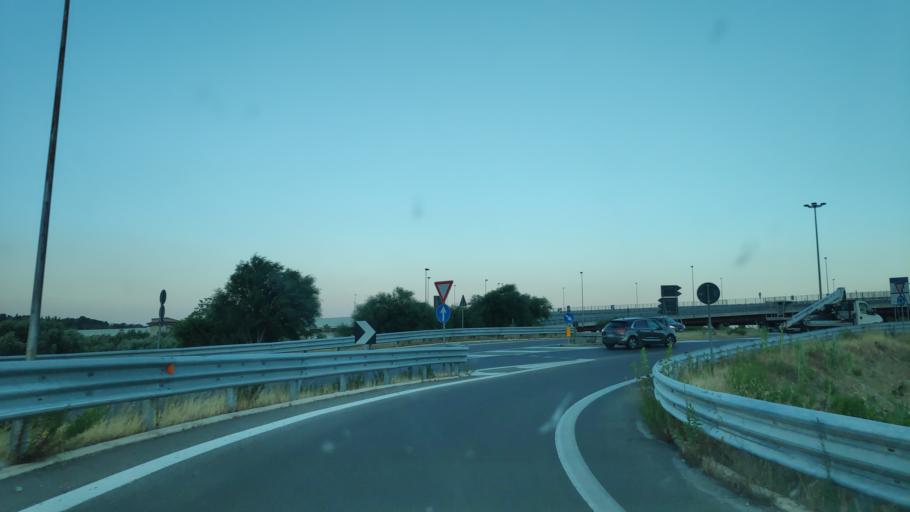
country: IT
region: Calabria
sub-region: Provincia di Reggio Calabria
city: Gioiosa Ionica
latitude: 38.3109
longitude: 16.3046
